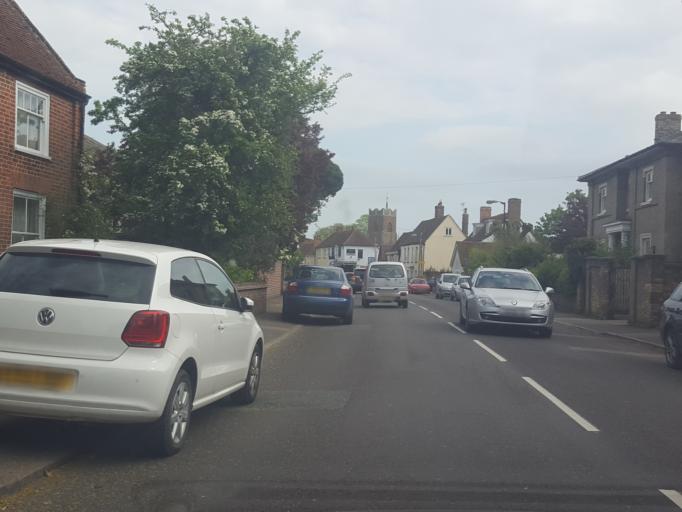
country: GB
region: England
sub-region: Essex
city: Little Clacton
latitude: 51.8587
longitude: 1.1604
